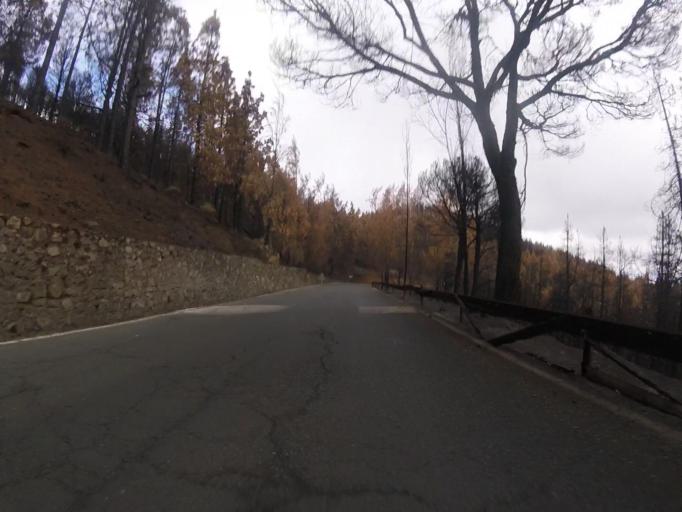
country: ES
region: Canary Islands
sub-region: Provincia de Las Palmas
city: Tejeda
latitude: 27.9801
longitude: -15.5801
